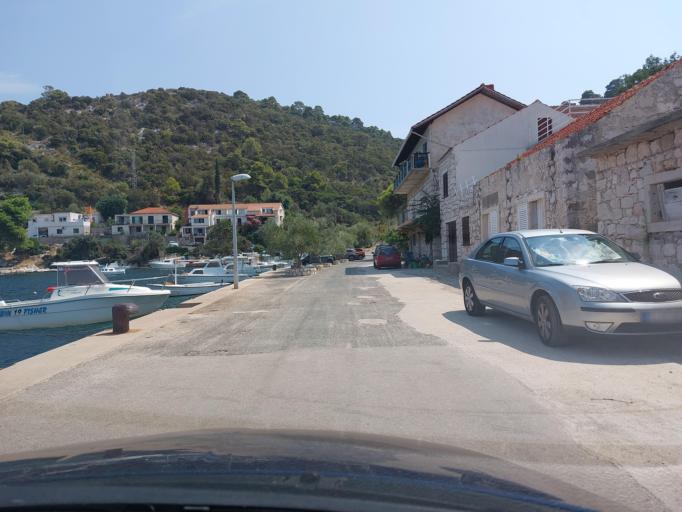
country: HR
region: Dubrovacko-Neretvanska
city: Smokvica
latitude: 42.7725
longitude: 16.8740
